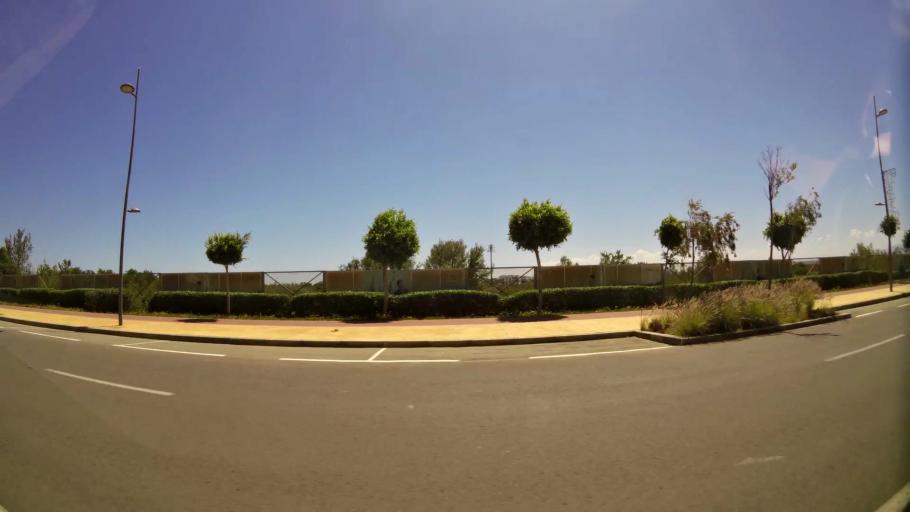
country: MA
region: Oriental
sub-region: Berkane-Taourirt
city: Madagh
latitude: 35.1040
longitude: -2.3003
